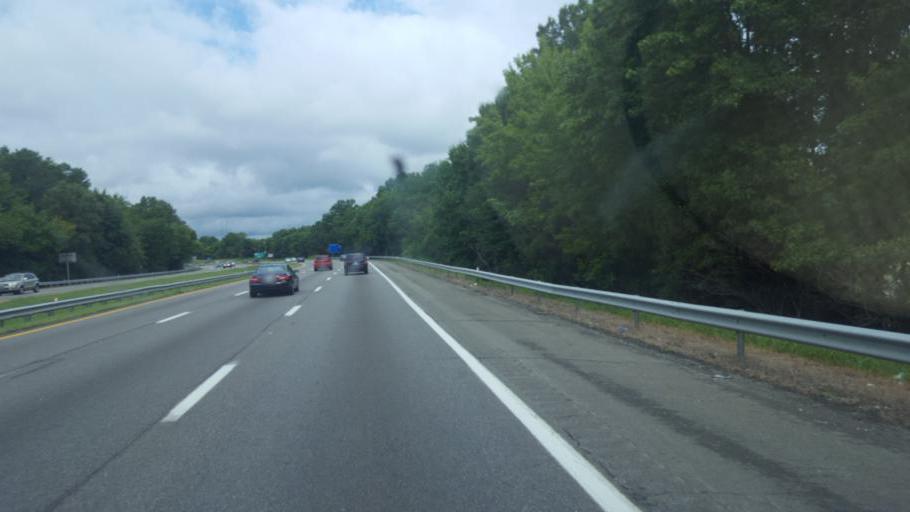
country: US
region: Virginia
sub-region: Henrico County
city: East Highland Park
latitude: 37.5510
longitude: -77.3996
